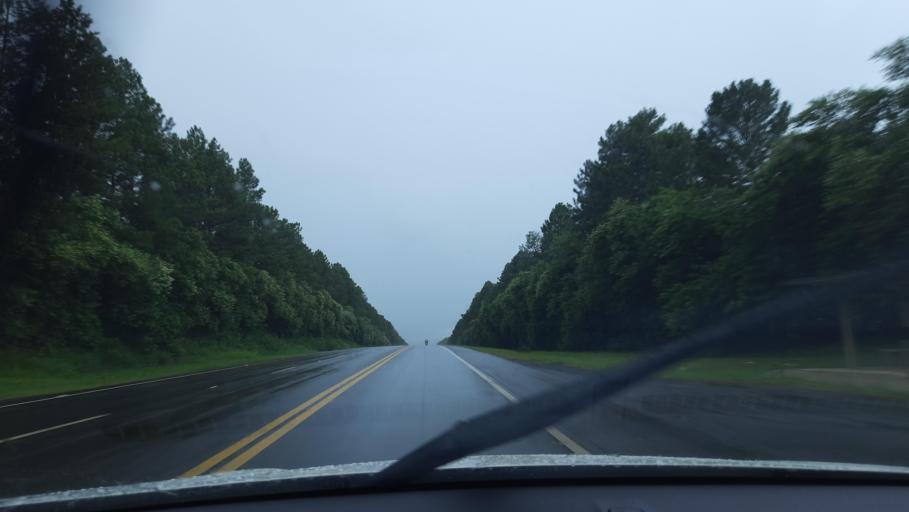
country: BR
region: Sao Paulo
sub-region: Casa Branca
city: Casa Branca
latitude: -21.7599
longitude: -47.0148
